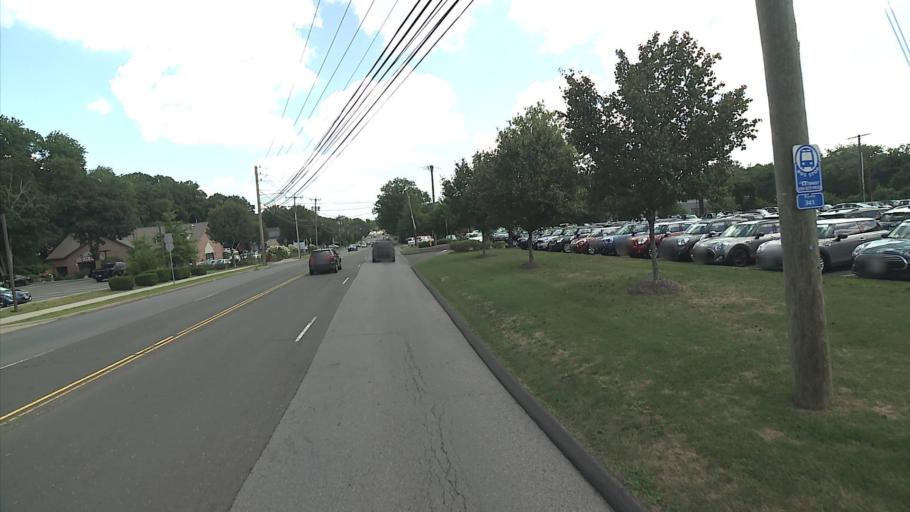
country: US
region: Connecticut
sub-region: Fairfield County
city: Darien
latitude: 41.0895
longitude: -73.4570
